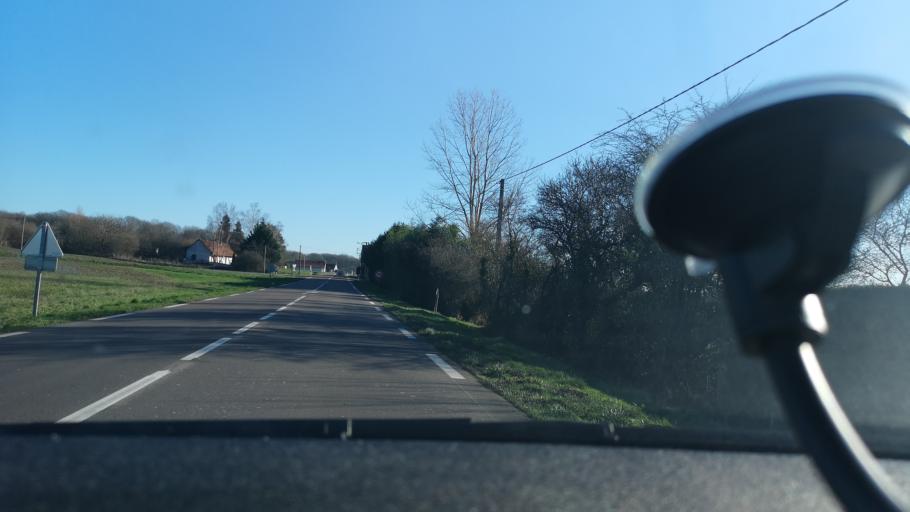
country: FR
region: Bourgogne
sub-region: Departement de Saone-et-Loire
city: Ouroux-sur-Saone
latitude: 46.7715
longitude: 4.9725
